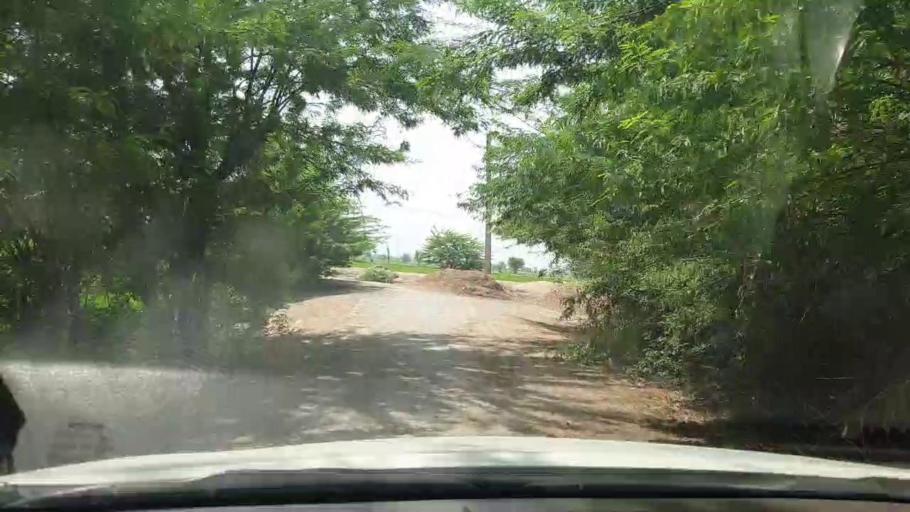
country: PK
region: Sindh
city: Shikarpur
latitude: 28.0187
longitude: 68.6485
